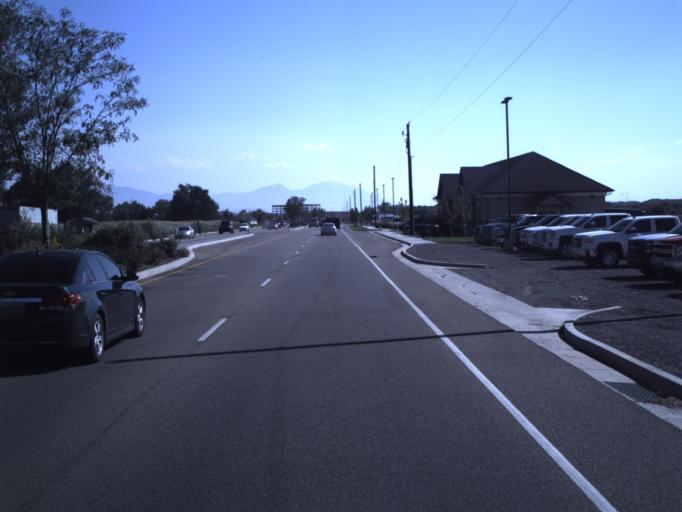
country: US
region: Utah
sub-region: Utah County
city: American Fork
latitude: 40.3670
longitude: -111.7692
